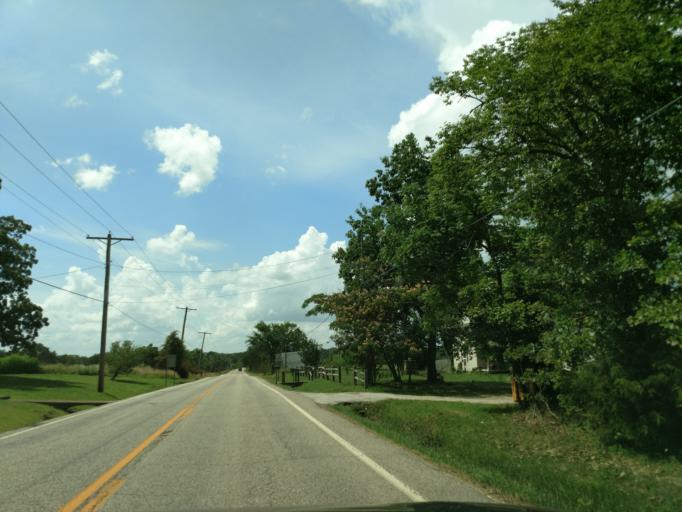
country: US
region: Arkansas
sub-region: Boone County
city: Harrison
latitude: 36.2558
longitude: -93.2244
